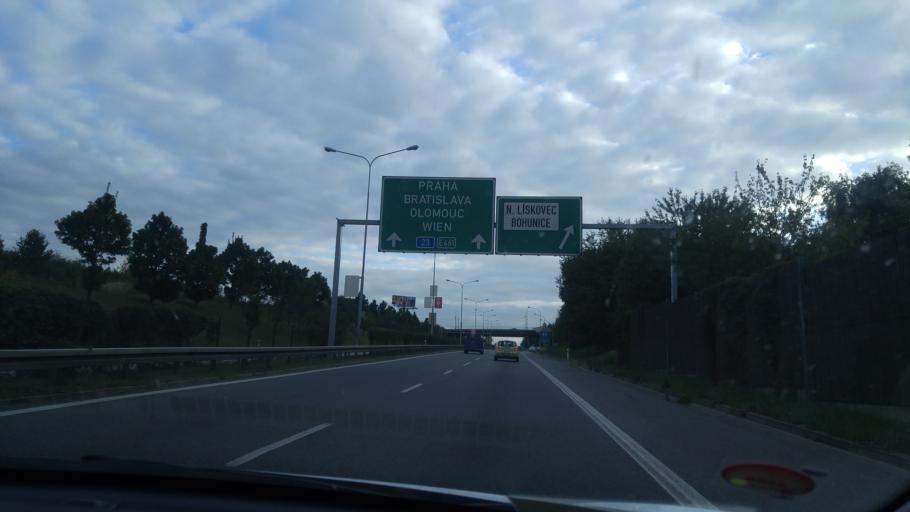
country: CZ
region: South Moravian
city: Ostopovice
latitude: 49.1810
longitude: 16.5644
